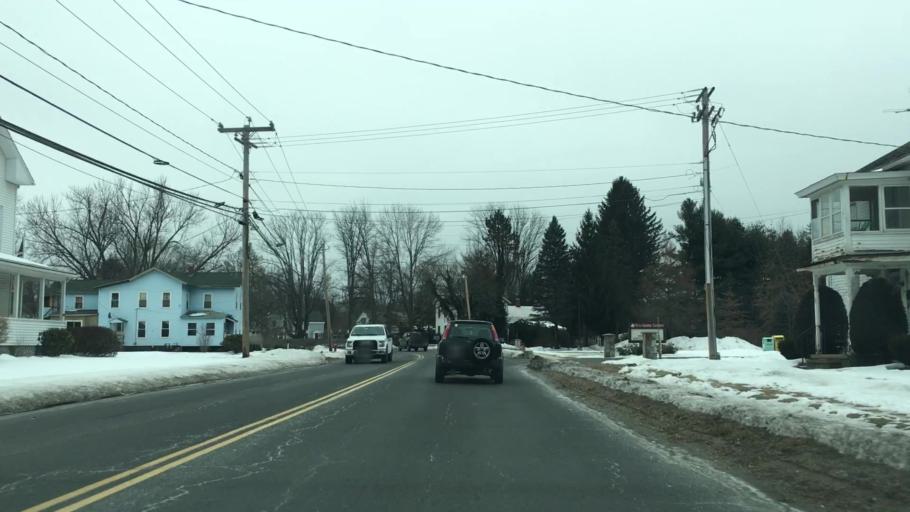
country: US
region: Massachusetts
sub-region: Hampden County
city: Westfield
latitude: 42.1300
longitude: -72.7328
